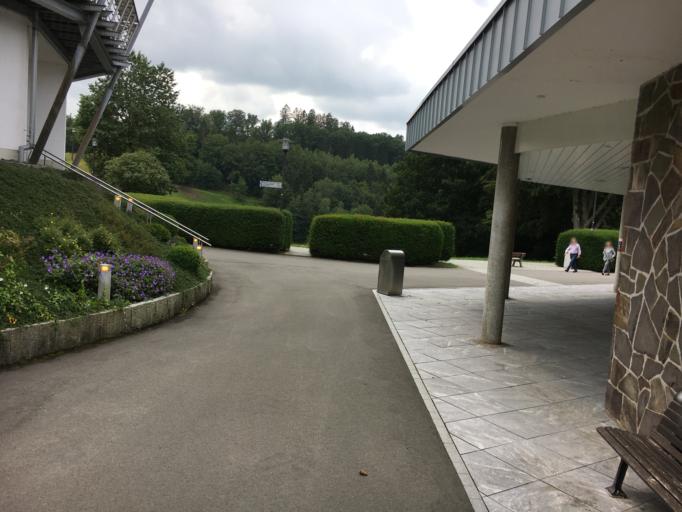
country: DE
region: North Rhine-Westphalia
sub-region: Regierungsbezirk Arnsberg
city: Attendorn
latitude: 51.1110
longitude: 7.8871
